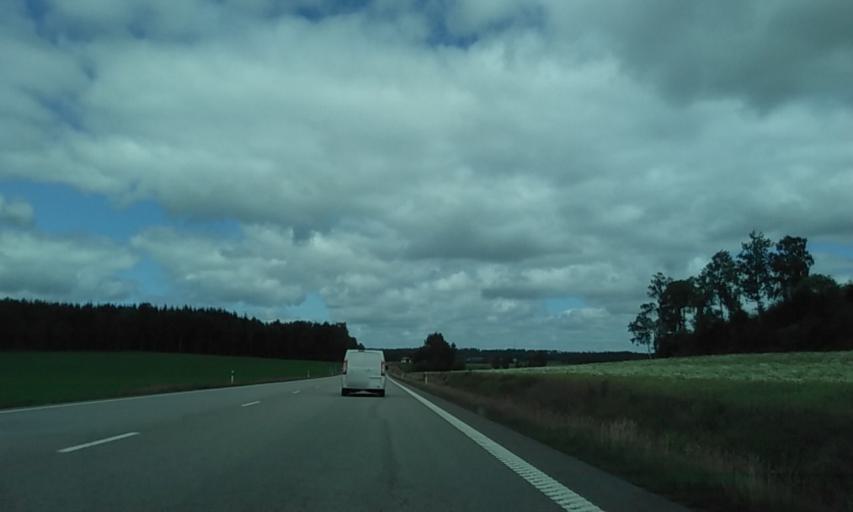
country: SE
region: Vaestra Goetaland
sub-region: Vargarda Kommun
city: Vargarda
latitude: 58.0653
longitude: 12.8173
